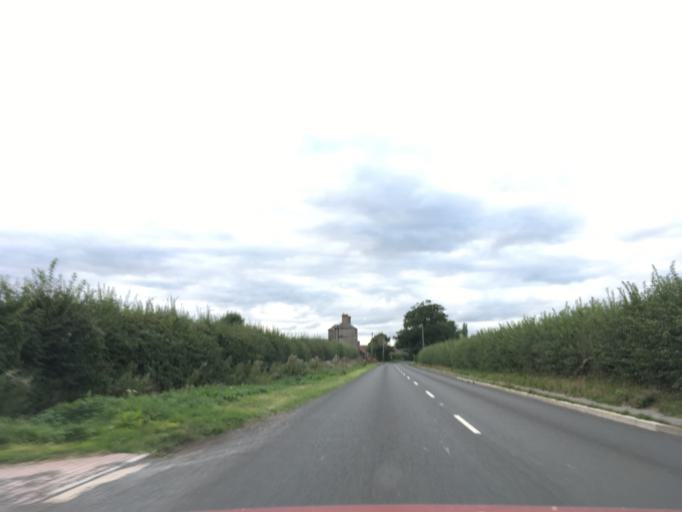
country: GB
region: England
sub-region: Wiltshire
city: Devizes
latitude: 51.3573
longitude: -2.0114
